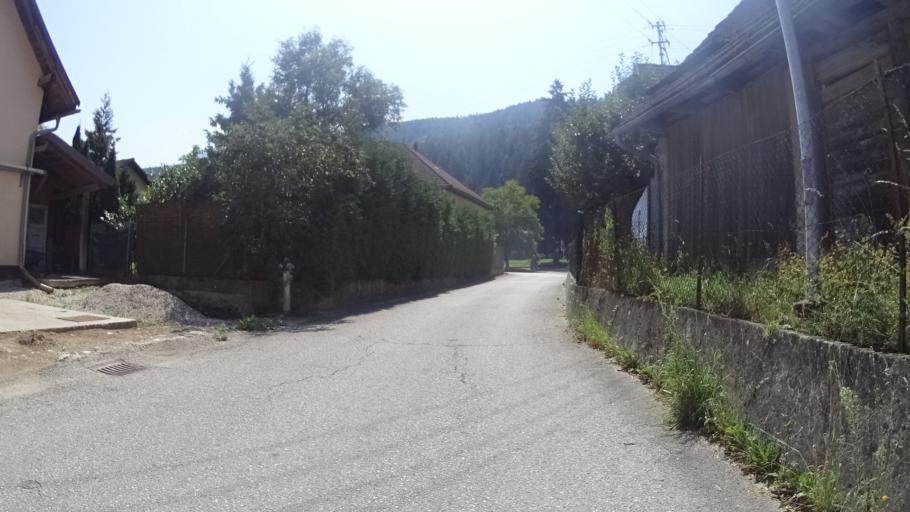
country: AT
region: Carinthia
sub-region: Politischer Bezirk Volkermarkt
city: Globasnitz
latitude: 46.5598
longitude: 14.6709
